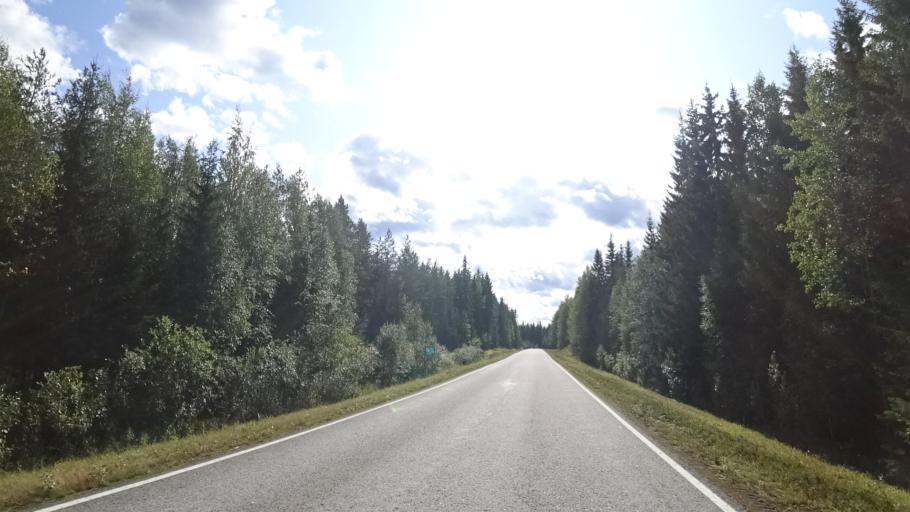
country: RU
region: Republic of Karelia
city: Vyartsilya
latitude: 62.2404
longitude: 30.7038
